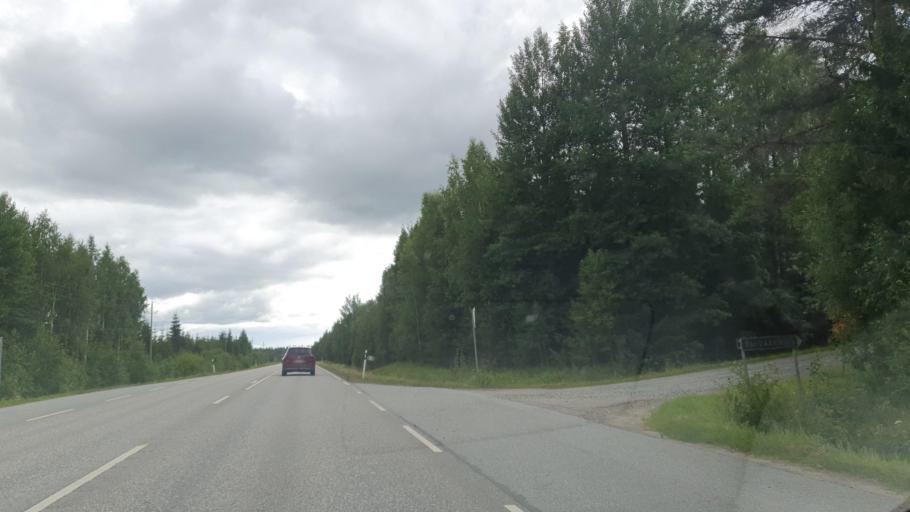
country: FI
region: Northern Savo
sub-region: Ylae-Savo
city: Sonkajaervi
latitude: 63.7153
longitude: 27.3632
